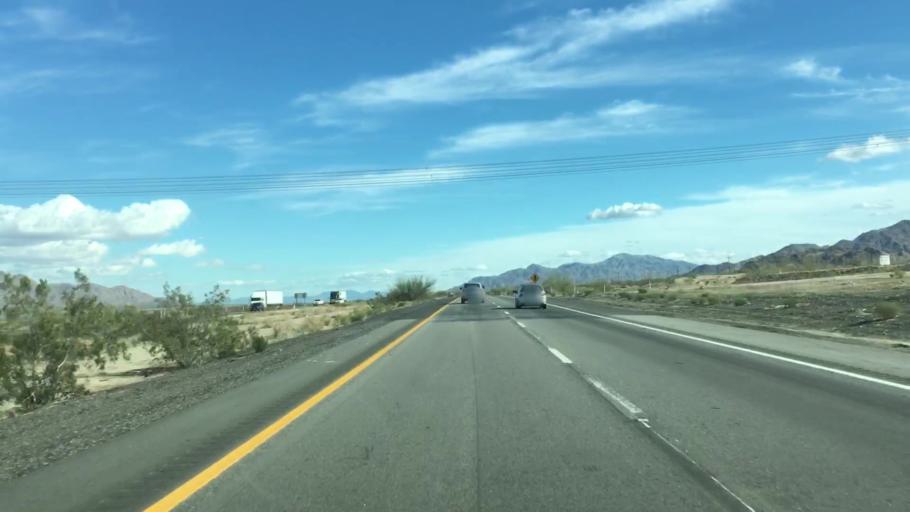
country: US
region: California
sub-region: Riverside County
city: Mecca
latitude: 33.6681
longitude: -115.6538
